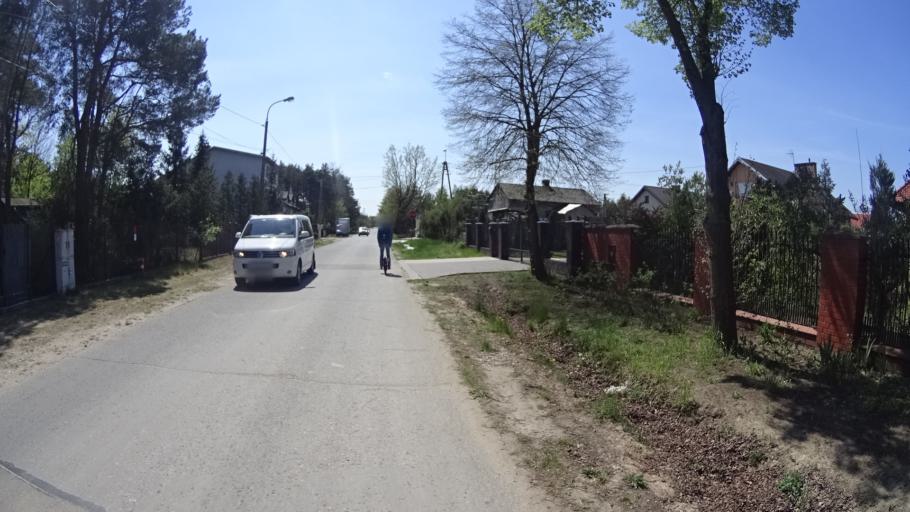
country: PL
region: Masovian Voivodeship
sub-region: Powiat warszawski zachodni
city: Truskaw
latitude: 52.2827
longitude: 20.7442
